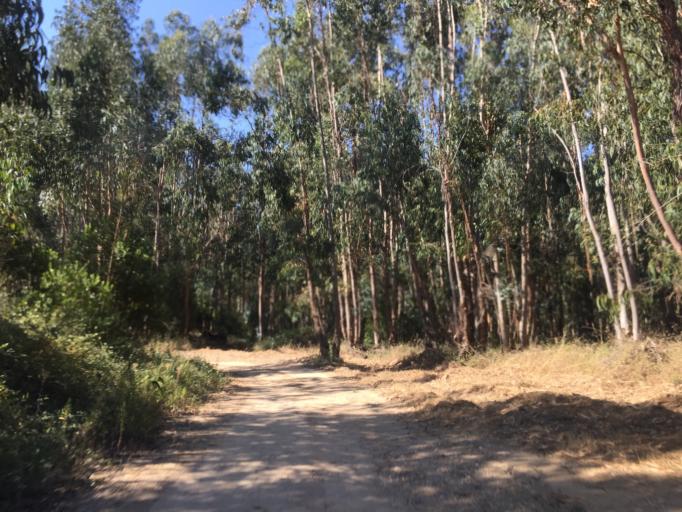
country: PT
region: Santarem
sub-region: Tomar
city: Tomar
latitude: 39.6125
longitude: -8.3536
